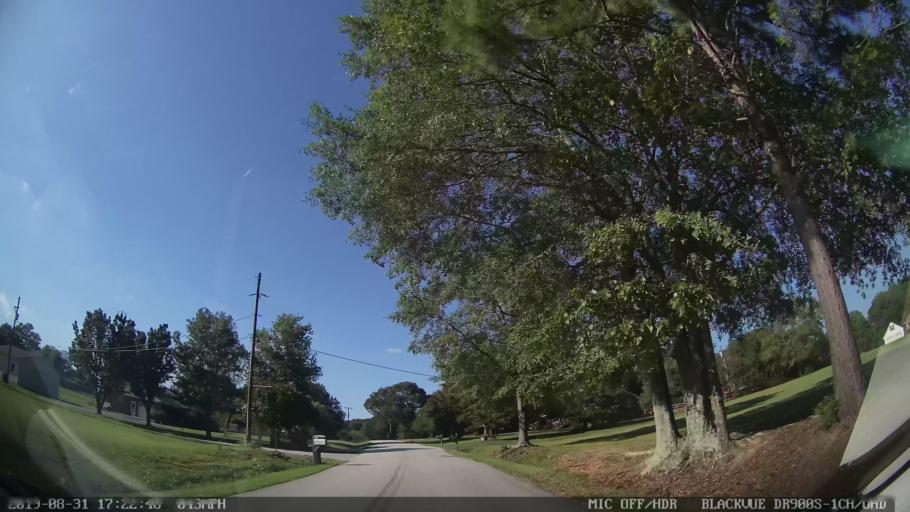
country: US
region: South Carolina
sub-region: Spartanburg County
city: Boiling Springs
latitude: 35.0791
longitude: -81.9380
